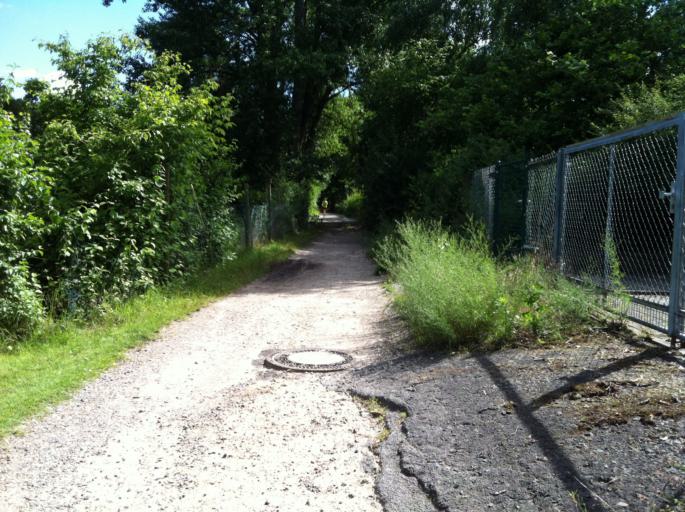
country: DE
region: Rheinland-Pfalz
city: Mainz
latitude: 50.0056
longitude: 8.2336
